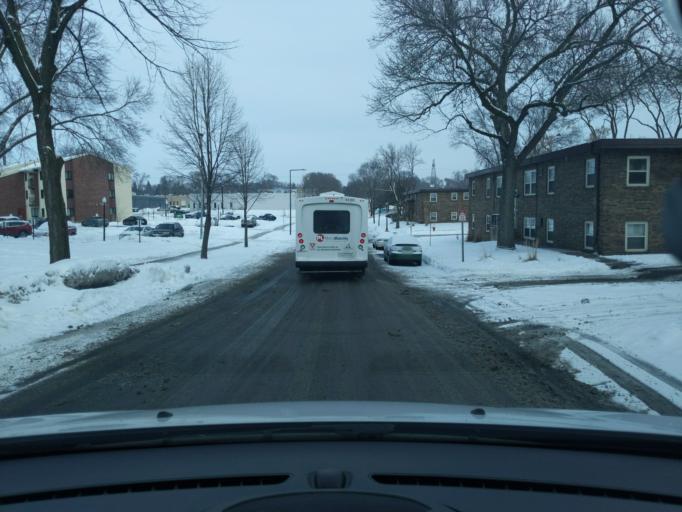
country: US
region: Minnesota
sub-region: Ramsey County
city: Falcon Heights
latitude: 44.9634
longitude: -93.1366
